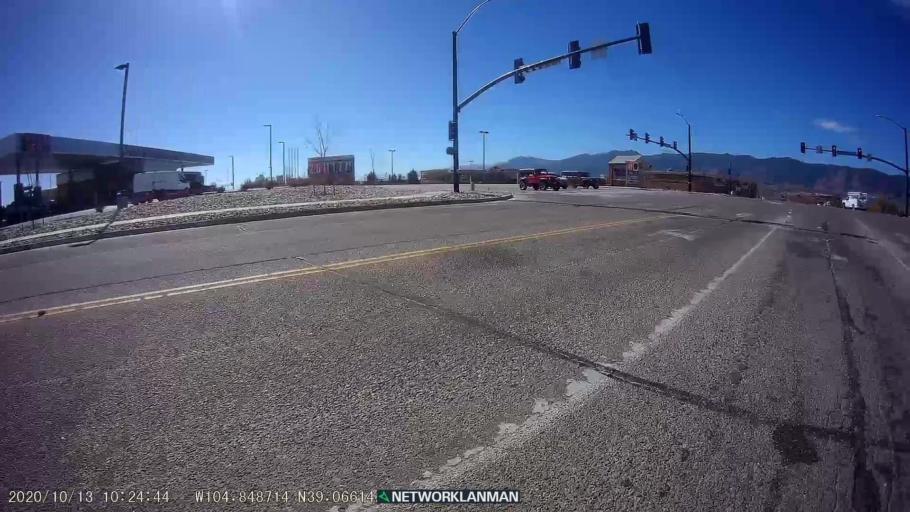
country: US
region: Colorado
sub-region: El Paso County
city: Gleneagle
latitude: 39.0662
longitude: -104.8488
